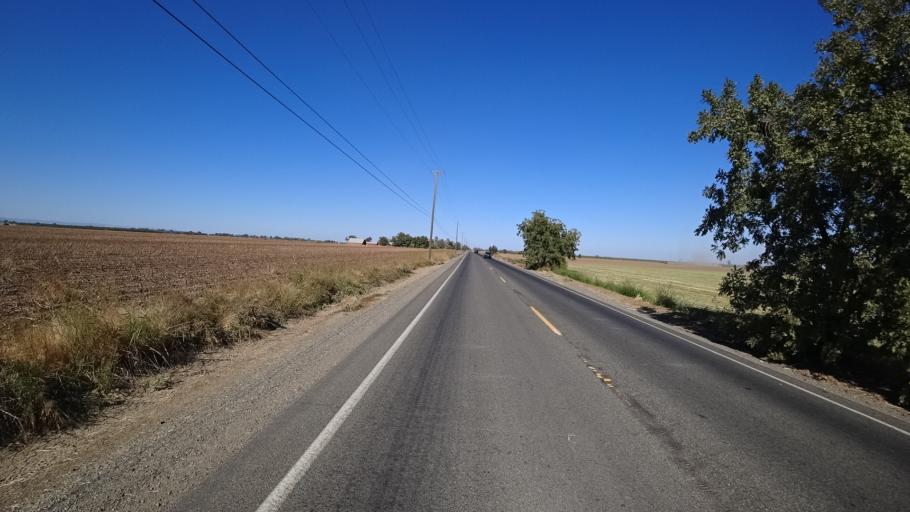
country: US
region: California
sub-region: Yolo County
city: Davis
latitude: 38.5645
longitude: -121.8033
